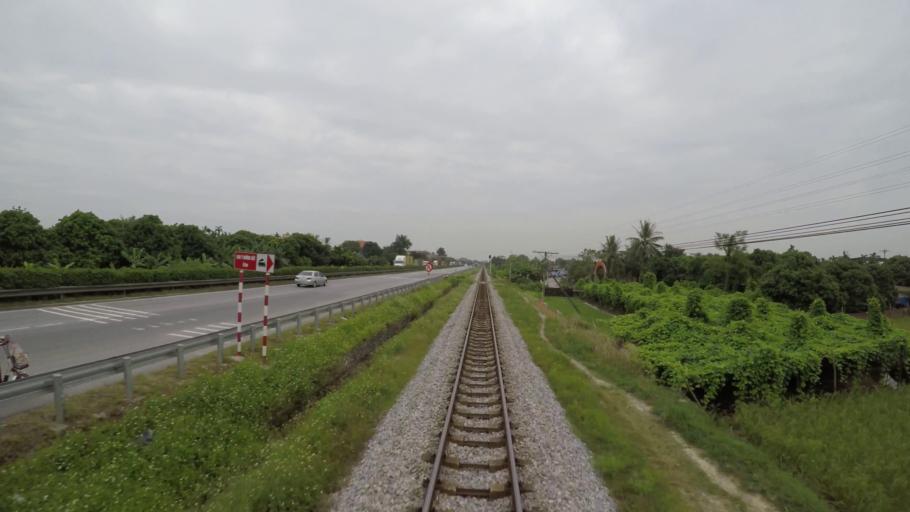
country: VN
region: Hai Duong
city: Phu Thai
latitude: 20.9699
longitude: 106.4453
